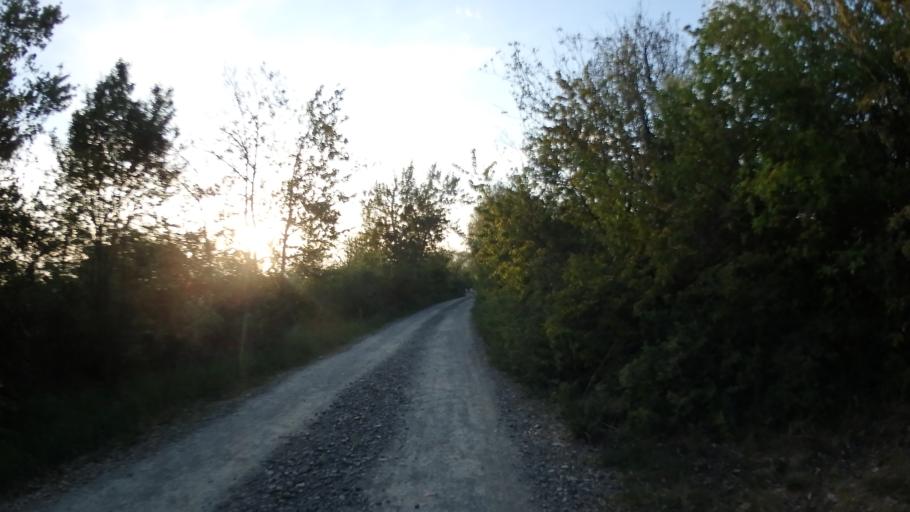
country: CZ
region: South Moravian
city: Ostopovice
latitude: 49.1472
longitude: 16.5517
